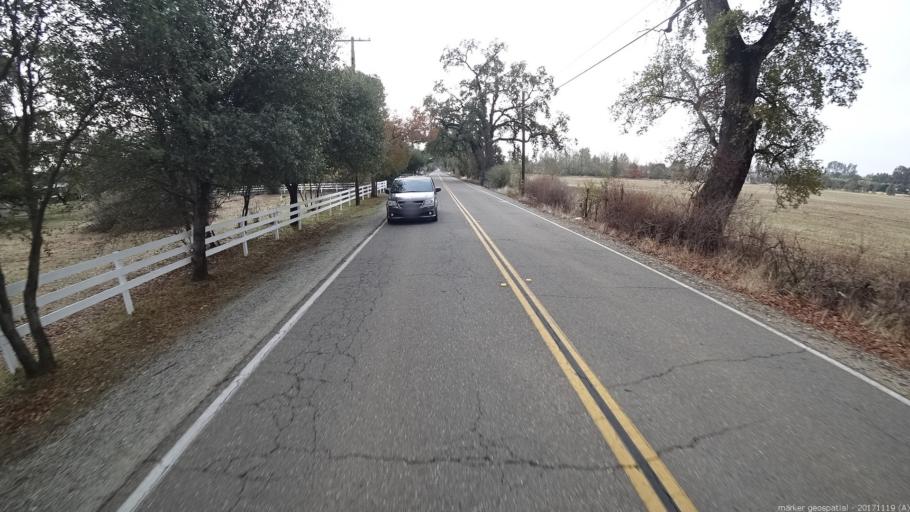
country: US
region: California
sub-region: Shasta County
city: Redding
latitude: 40.5329
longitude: -122.3338
